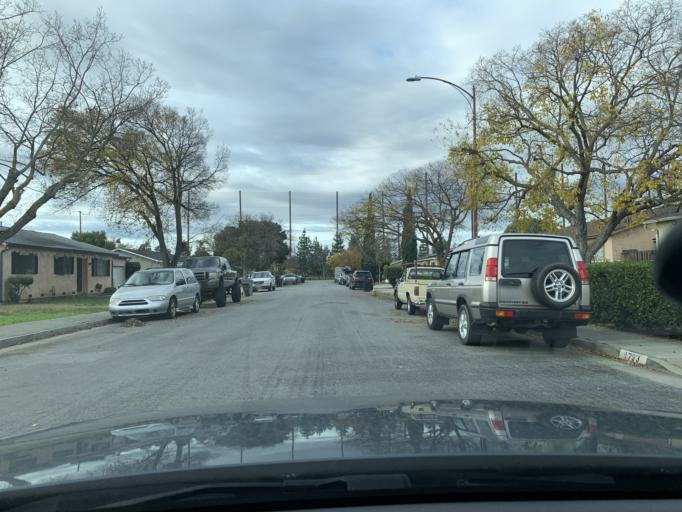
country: US
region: California
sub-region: Santa Clara County
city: Alum Rock
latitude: 37.3485
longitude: -121.8495
